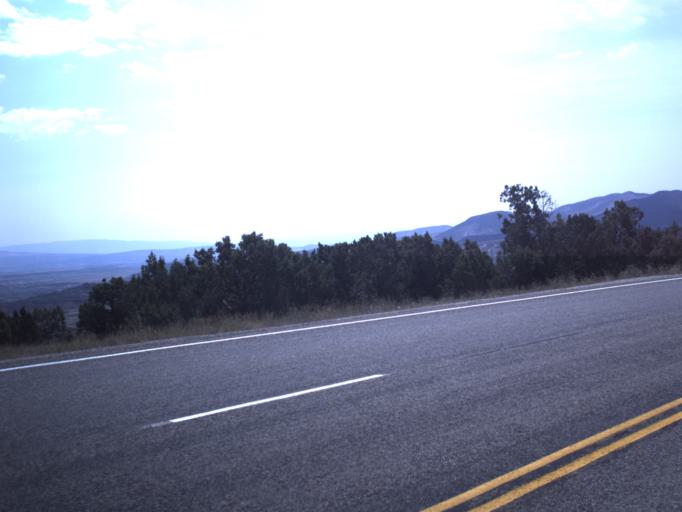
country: US
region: Utah
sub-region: Uintah County
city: Vernal
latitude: 40.6226
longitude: -109.4732
